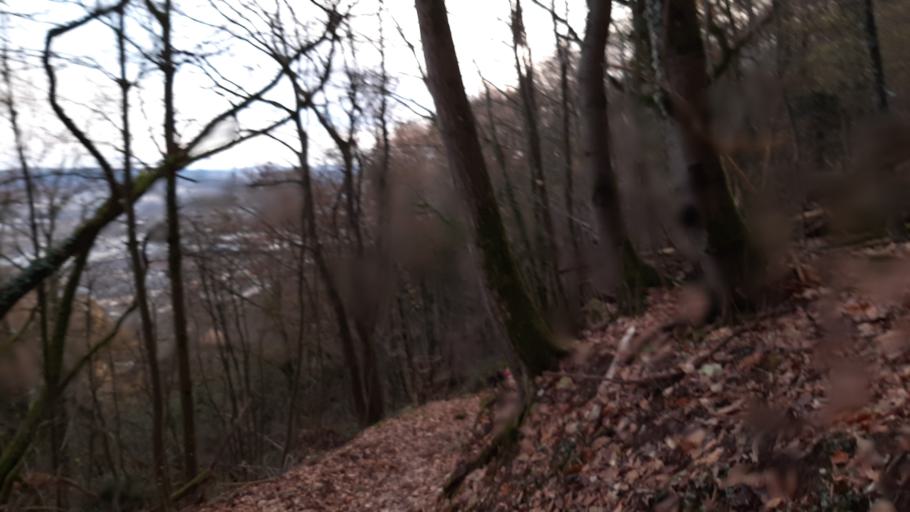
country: DE
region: Rheinland-Pfalz
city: Trier
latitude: 49.7555
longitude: 6.6147
